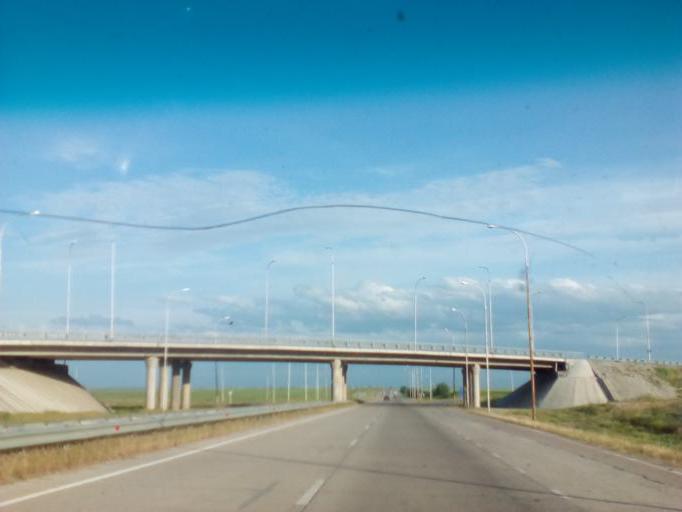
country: KZ
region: Ongtustik Qazaqstan
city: Temirlanovka
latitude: 42.5493
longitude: 69.3222
